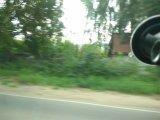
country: RU
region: Moskovskaya
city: Zhukovskiy
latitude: 55.6054
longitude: 38.1264
